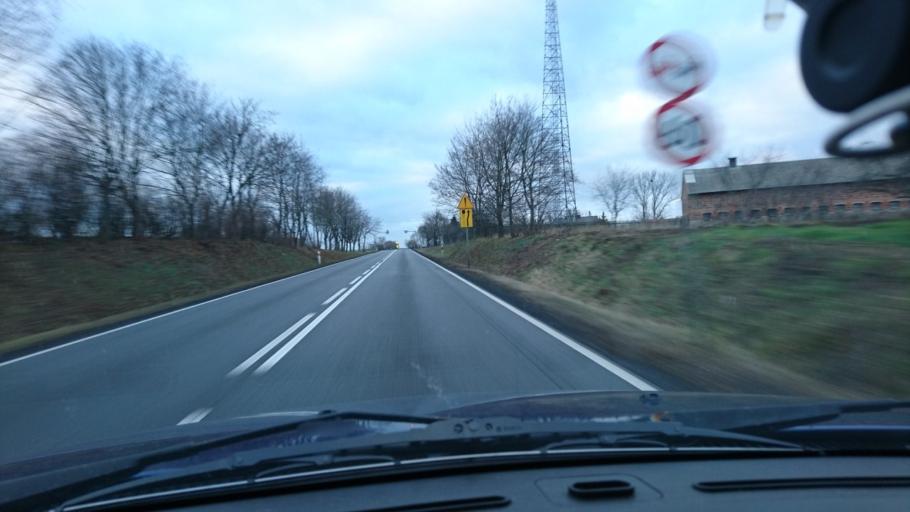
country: PL
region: Greater Poland Voivodeship
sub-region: Powiat kepinski
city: Opatow
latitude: 51.2123
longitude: 18.1436
